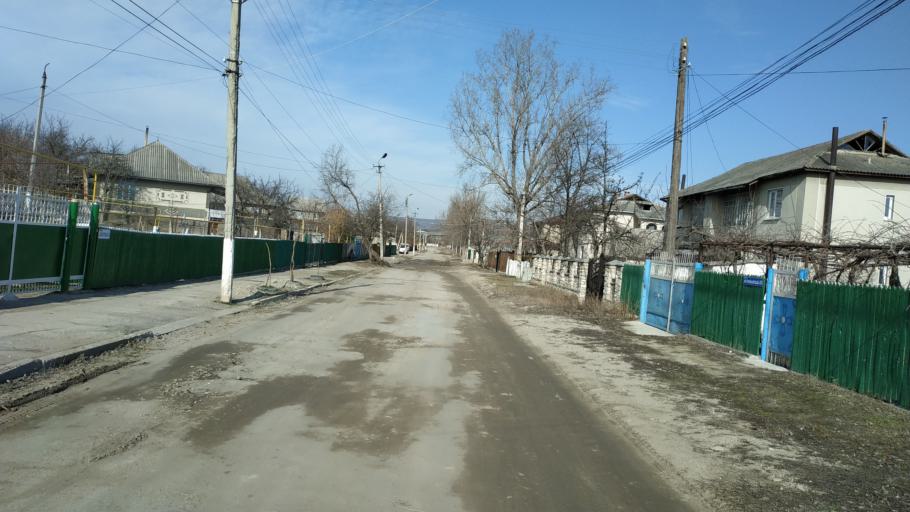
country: MD
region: Nisporeni
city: Nisporeni
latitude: 47.0693
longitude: 28.1744
